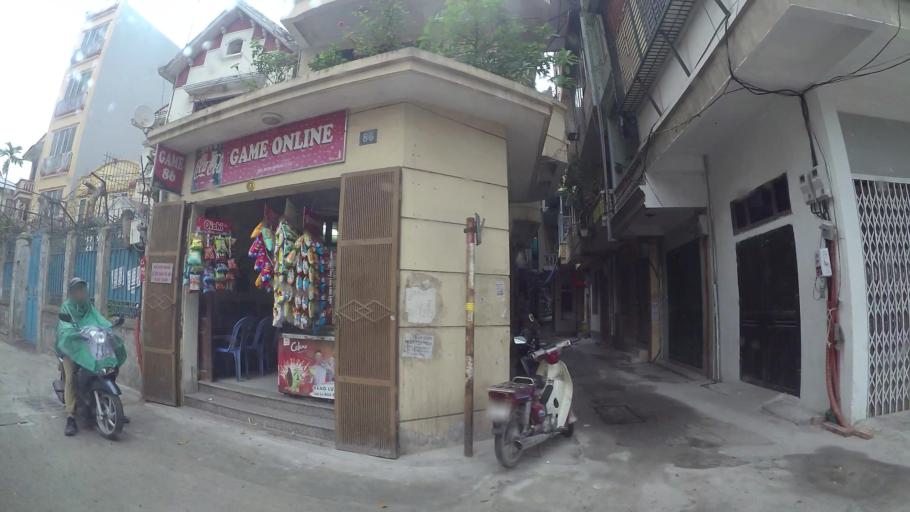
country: VN
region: Ha Noi
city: Dong Da
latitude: 21.0199
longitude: 105.8230
